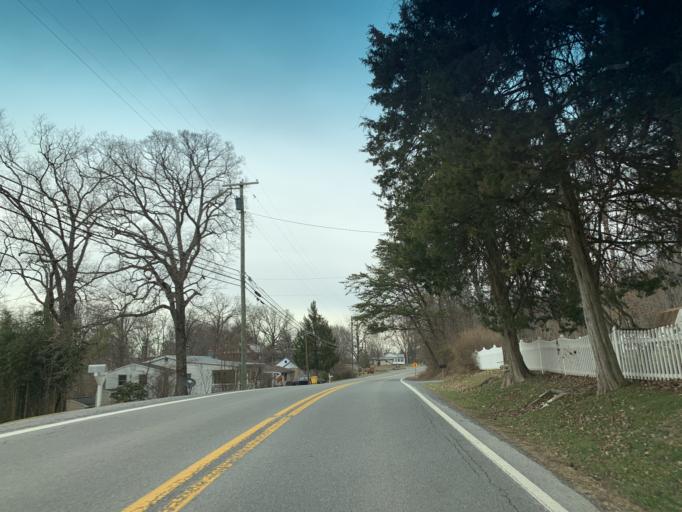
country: US
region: West Virginia
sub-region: Jefferson County
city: Shannondale
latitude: 39.2504
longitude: -77.7798
